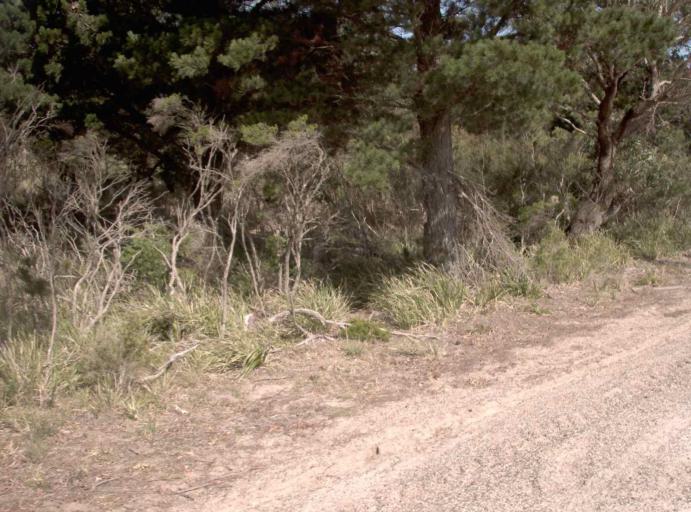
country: AU
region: Victoria
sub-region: Wellington
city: Sale
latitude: -38.3288
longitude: 147.1629
